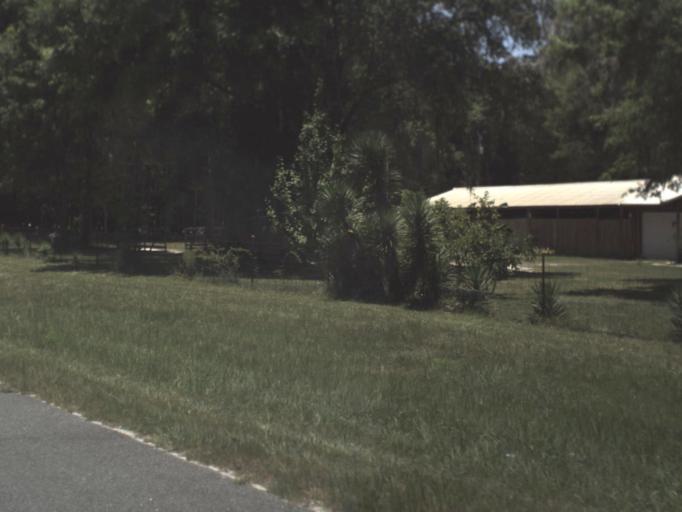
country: US
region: Florida
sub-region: Dixie County
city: Cross City
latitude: 29.6702
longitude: -82.9842
